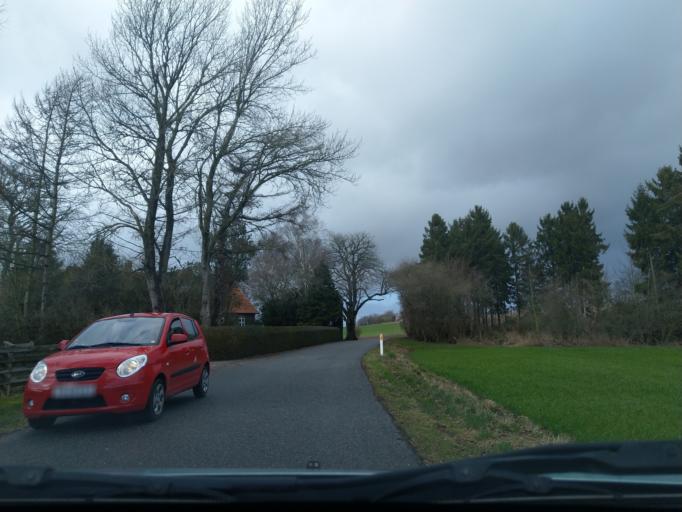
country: DK
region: Zealand
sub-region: Naestved Kommune
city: Fuglebjerg
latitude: 55.3415
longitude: 11.5854
